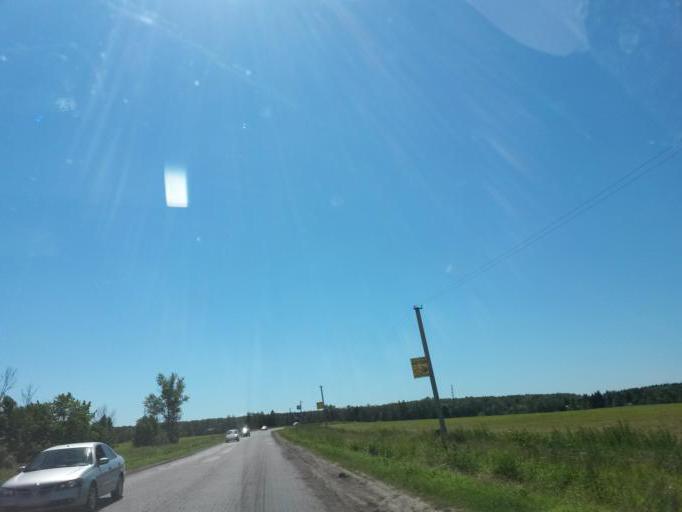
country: RU
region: Moskovskaya
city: Lyubuchany
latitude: 55.2515
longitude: 37.5936
